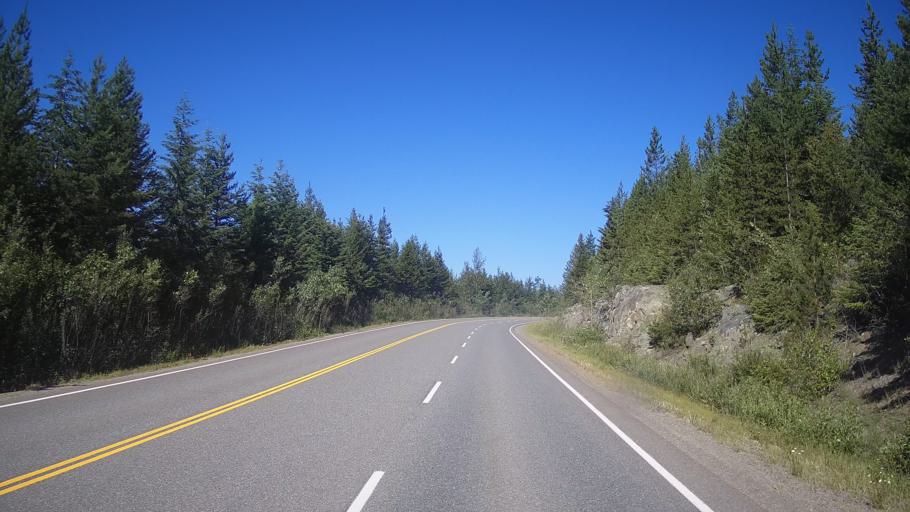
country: CA
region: British Columbia
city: Kamloops
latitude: 51.4940
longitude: -120.3316
